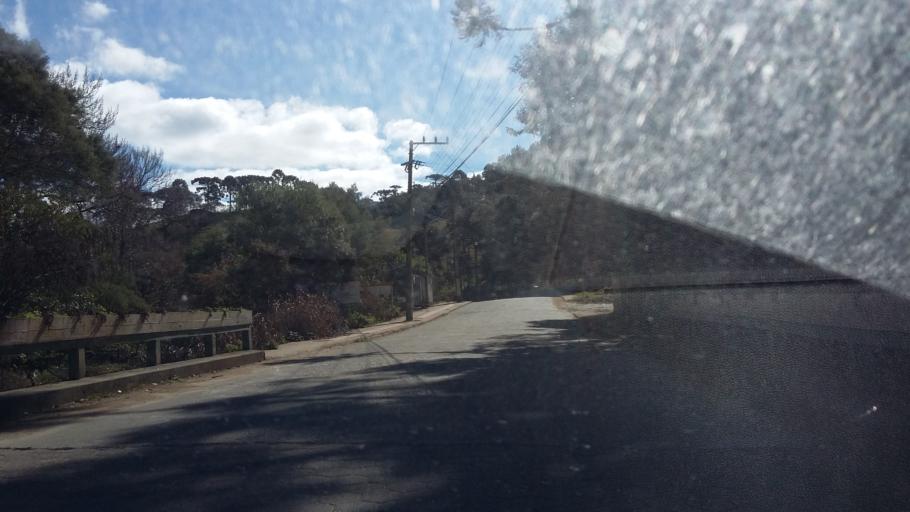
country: BR
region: Santa Catarina
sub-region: Santo Amaro Da Imperatriz
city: Santo Amaro da Imperatriz
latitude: -27.6787
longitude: -49.0067
